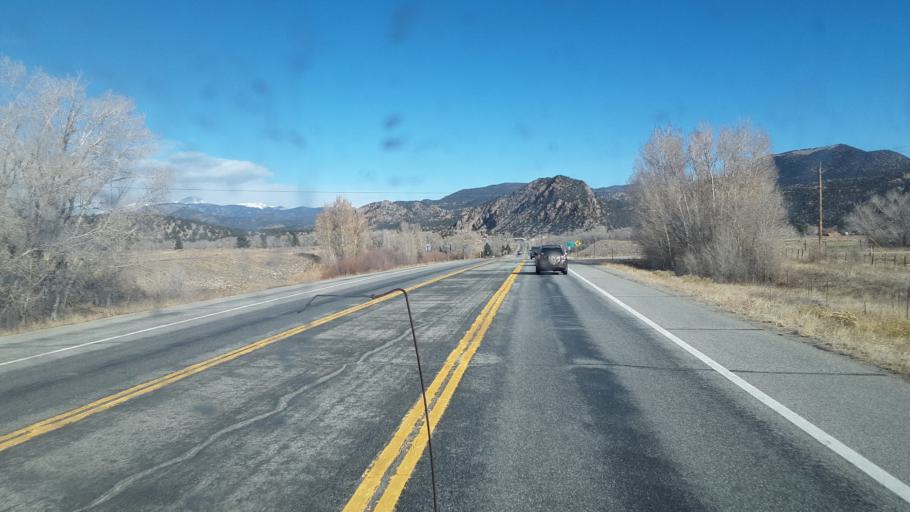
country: US
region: Colorado
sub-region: Chaffee County
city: Buena Vista
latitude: 38.7368
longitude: -106.0852
